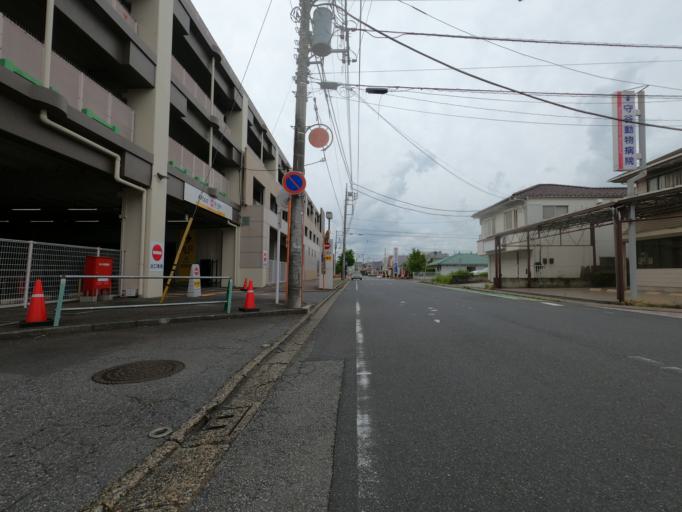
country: JP
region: Ibaraki
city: Moriya
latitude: 35.9683
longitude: 139.9741
